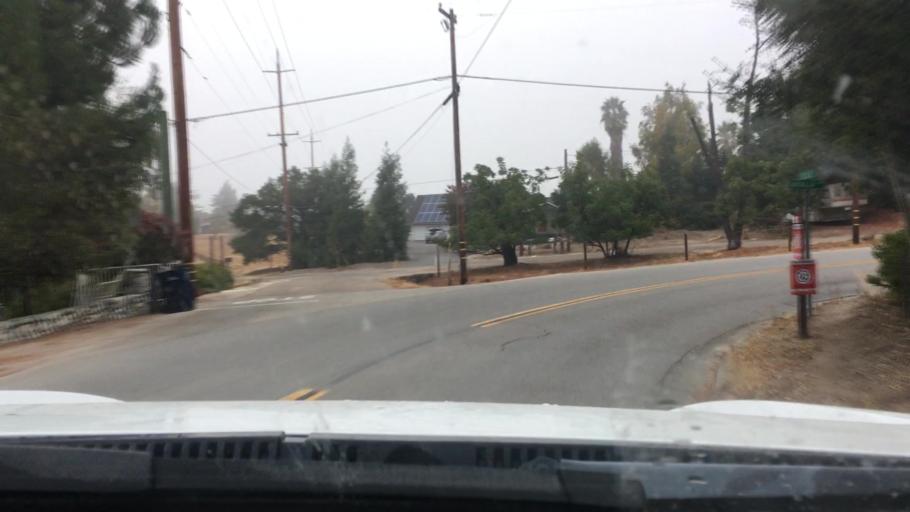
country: US
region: California
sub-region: San Luis Obispo County
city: Atascadero
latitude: 35.4901
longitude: -120.6874
